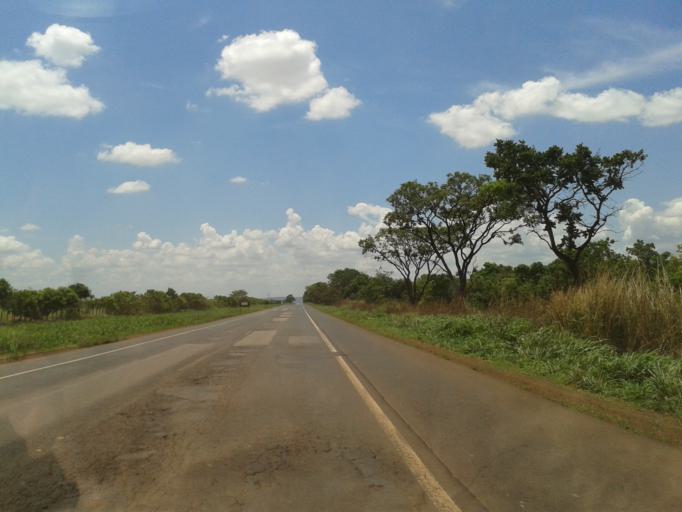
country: BR
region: Goias
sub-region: Goiatuba
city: Goiatuba
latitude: -18.2712
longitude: -49.6433
